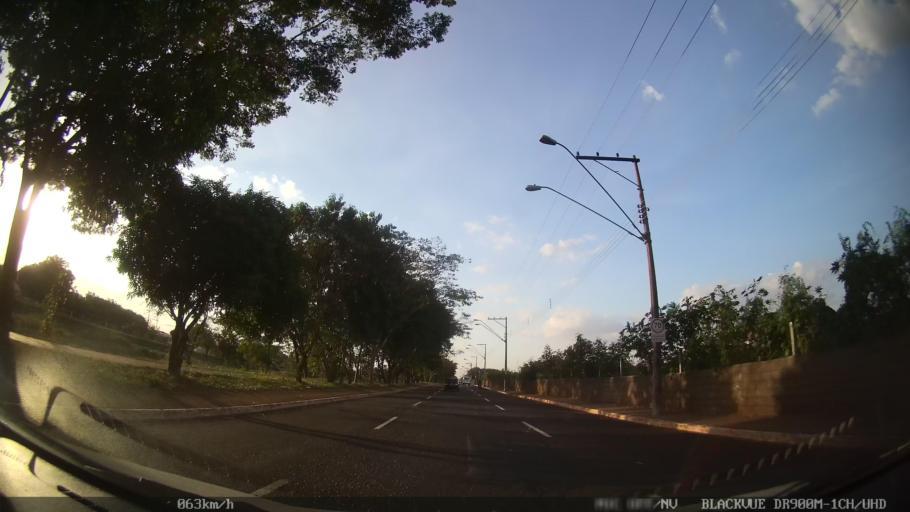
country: BR
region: Sao Paulo
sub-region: Ribeirao Preto
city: Ribeirao Preto
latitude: -21.1323
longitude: -47.8033
